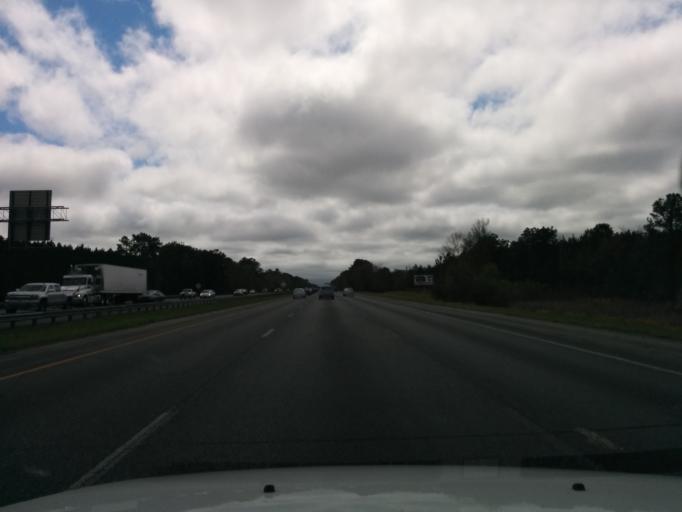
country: US
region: Georgia
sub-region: Chatham County
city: Pooler
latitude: 32.0577
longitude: -81.2545
